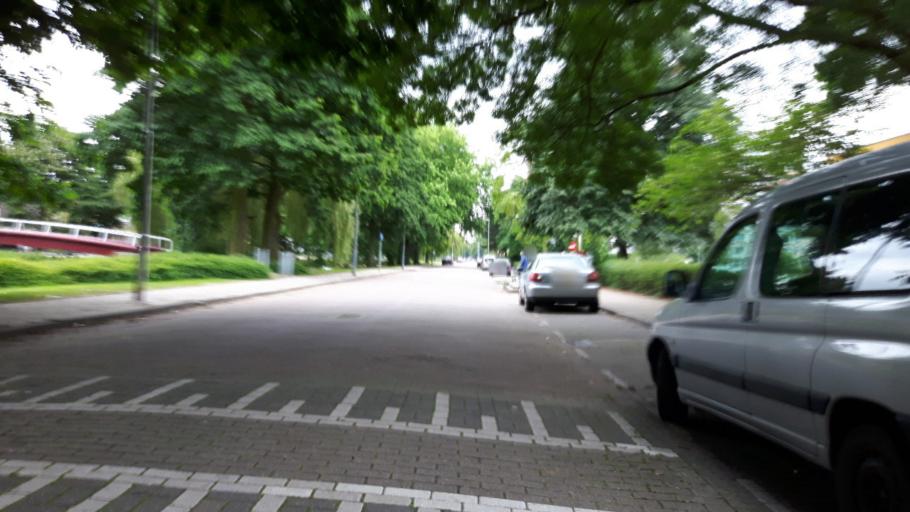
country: NL
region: South Holland
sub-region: Gemeente Rotterdam
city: Rotterdam
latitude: 51.9571
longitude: 4.4687
